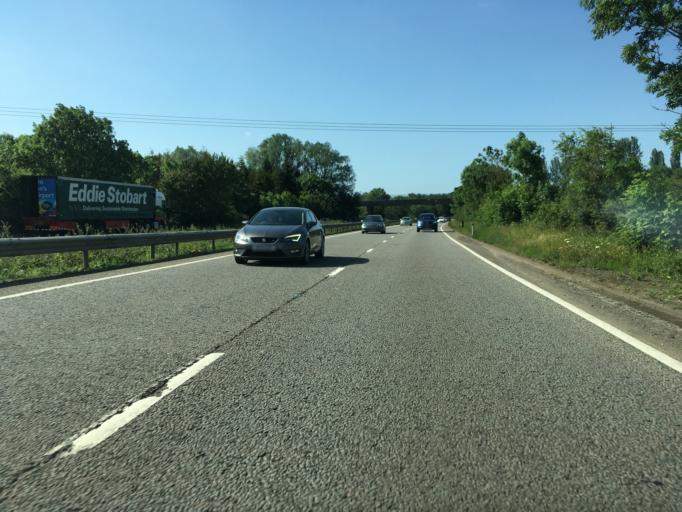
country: GB
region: England
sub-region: Milton Keynes
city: Water Eaton
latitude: 51.9994
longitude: -0.7082
